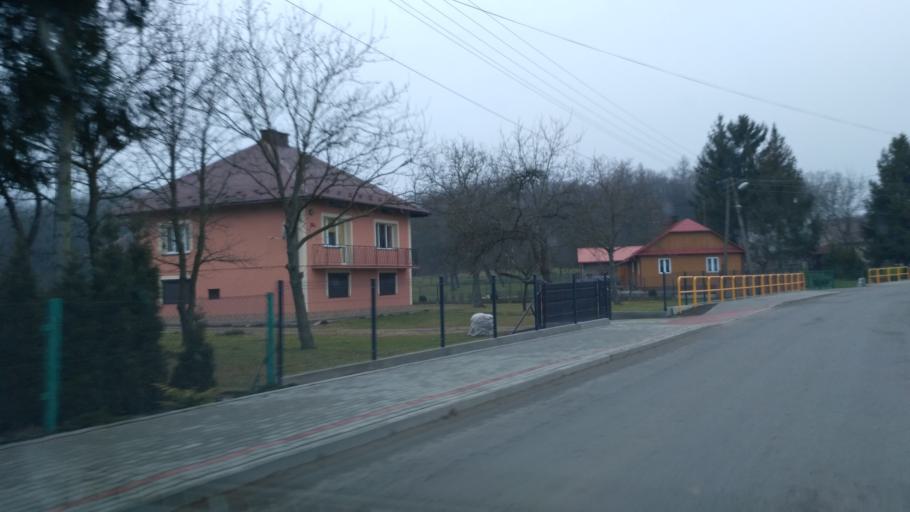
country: PL
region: Subcarpathian Voivodeship
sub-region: Powiat jaroslawski
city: Pawlosiow
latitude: 49.9826
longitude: 22.6336
